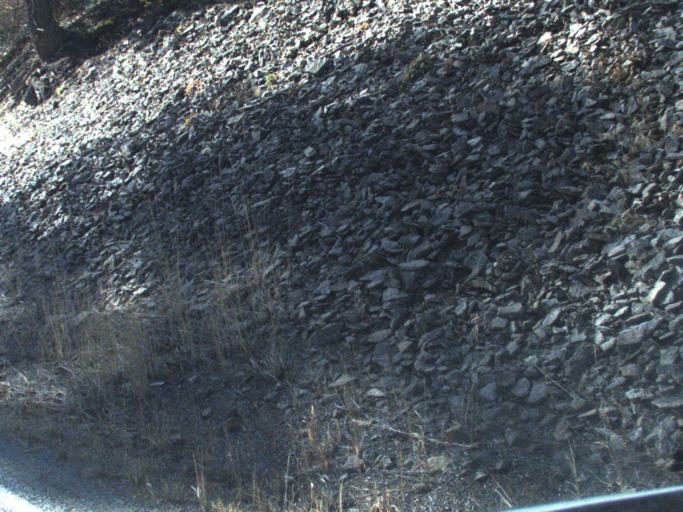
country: US
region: Washington
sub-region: Ferry County
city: Republic
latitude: 48.7292
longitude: -118.6541
